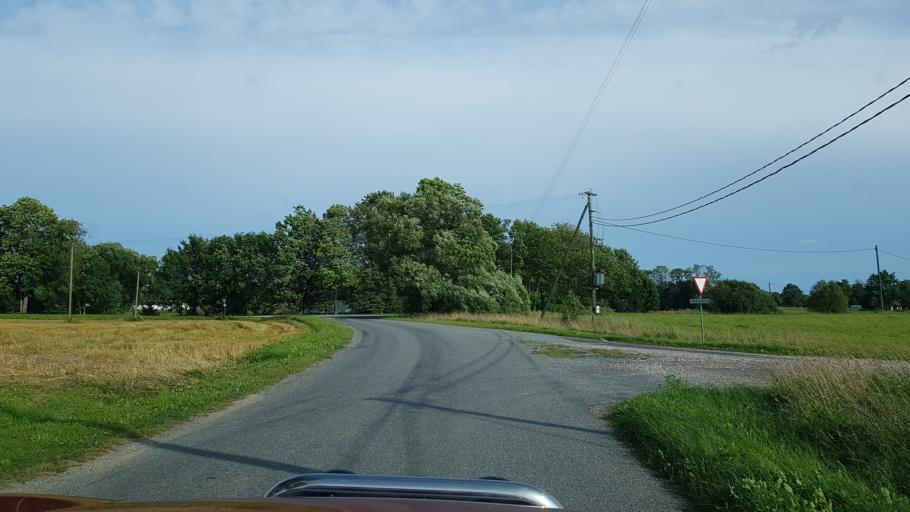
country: EE
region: Laeaene
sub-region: Lihula vald
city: Lihula
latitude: 58.4483
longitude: 24.0001
